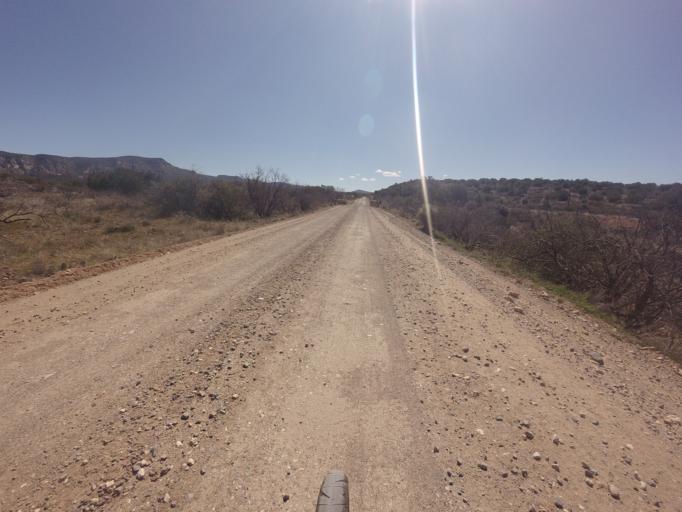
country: US
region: Arizona
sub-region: Yavapai County
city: Lake Montezuma
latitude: 34.6433
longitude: -111.7202
